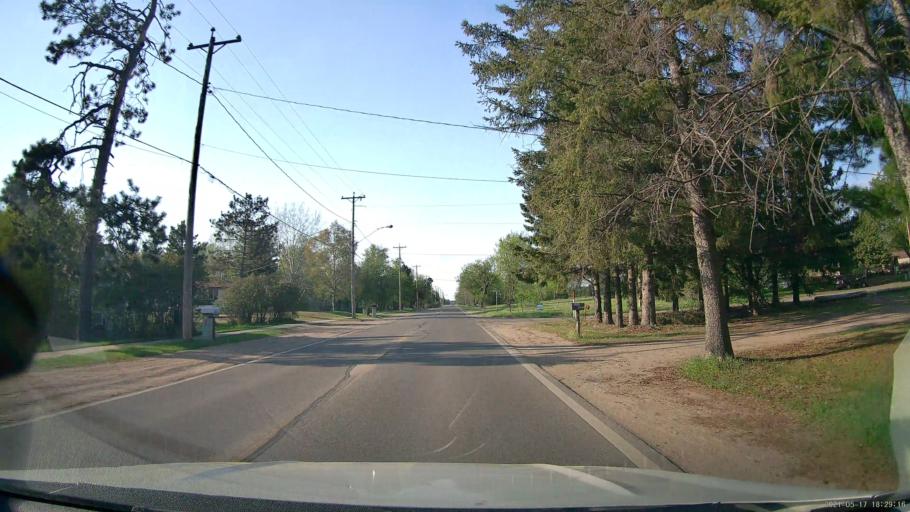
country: US
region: Minnesota
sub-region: Hubbard County
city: Park Rapids
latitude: 46.9249
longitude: -95.0477
